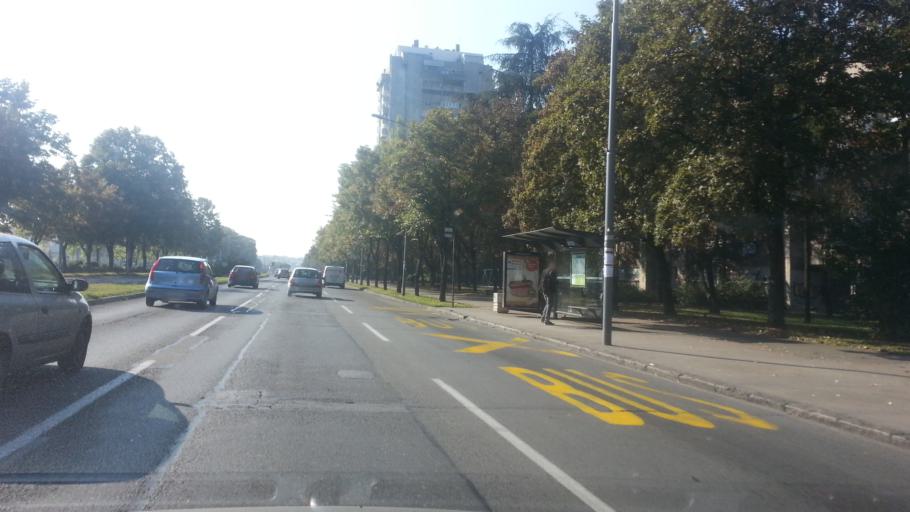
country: RS
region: Central Serbia
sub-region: Belgrade
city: Zemun
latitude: 44.8335
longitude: 20.4184
